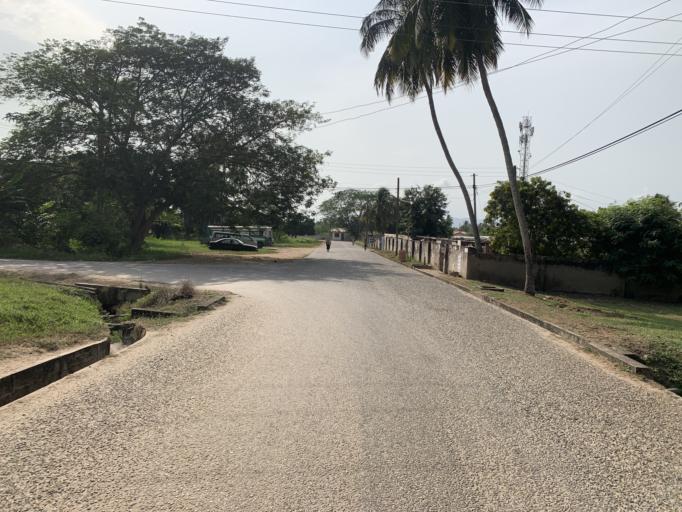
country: GH
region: Central
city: Winneba
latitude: 5.3400
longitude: -0.6271
